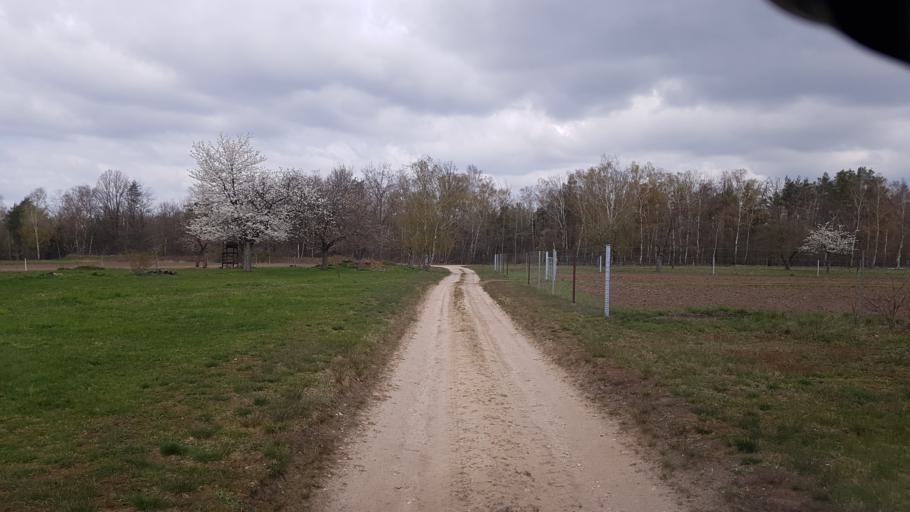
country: DE
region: Brandenburg
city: Hohenleipisch
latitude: 51.5056
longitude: 13.5475
